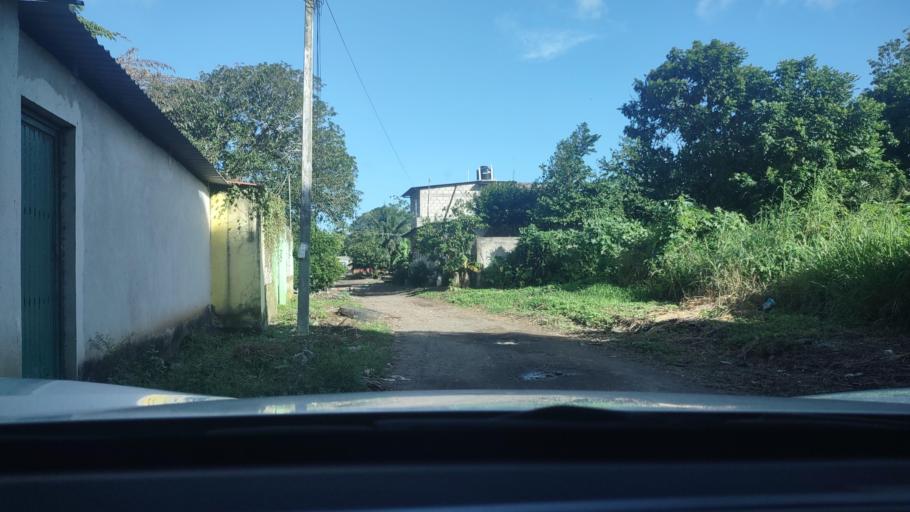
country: MX
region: Veracruz
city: El Tejar
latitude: 19.0721
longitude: -96.1577
